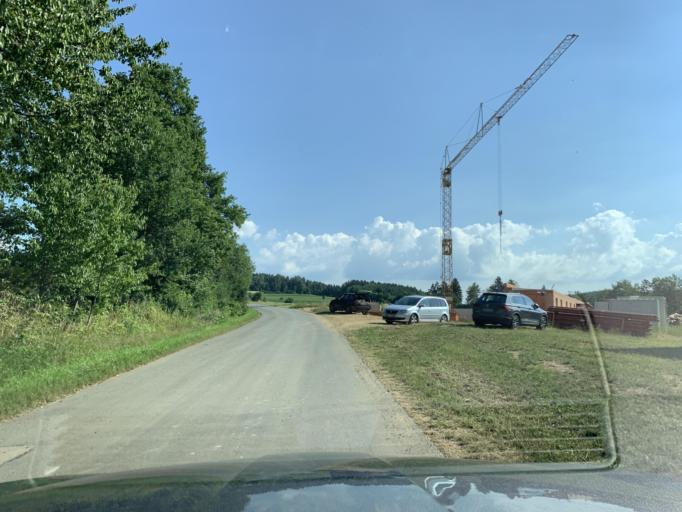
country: DE
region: Bavaria
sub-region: Upper Palatinate
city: Dieterskirchen
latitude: 49.4165
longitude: 12.4296
